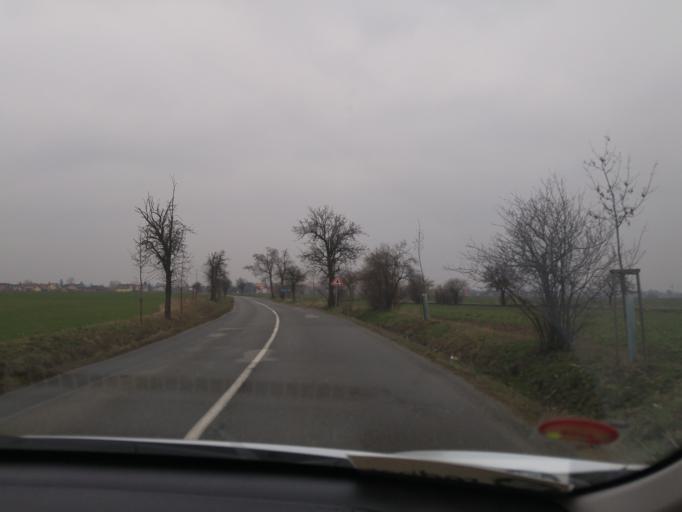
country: CZ
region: Central Bohemia
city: Brandys nad Labem-Stara Boleslav
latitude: 50.1957
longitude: 14.6385
